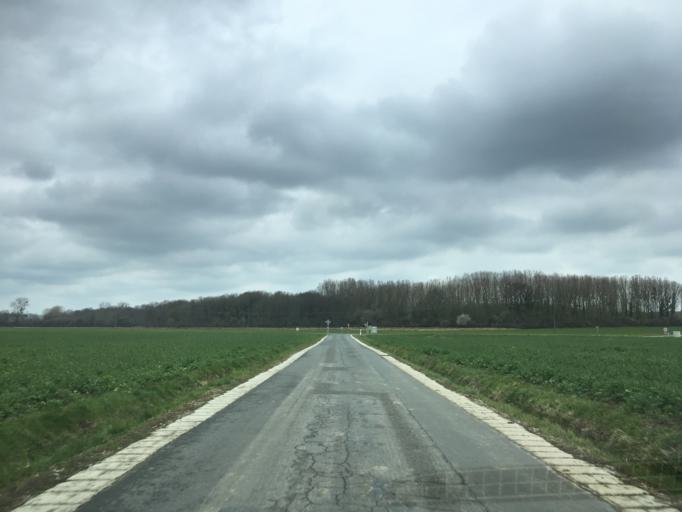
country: FR
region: Centre
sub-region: Departement d'Indre-et-Loire
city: Chanceaux-sur-Choisille
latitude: 47.4745
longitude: 0.7242
